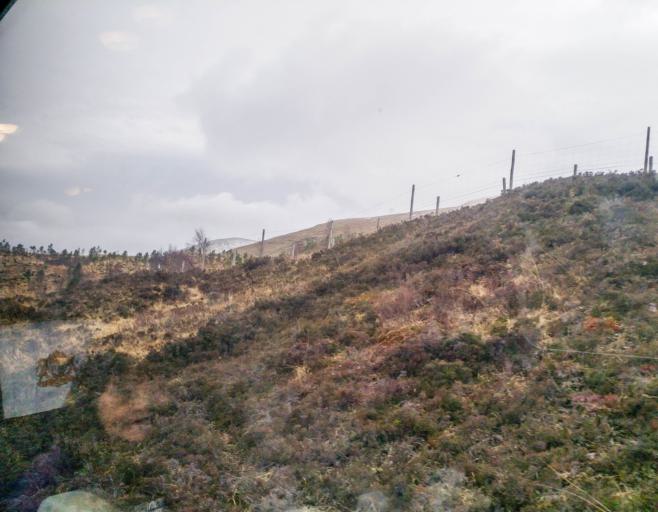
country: GB
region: Scotland
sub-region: Highland
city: Spean Bridge
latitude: 56.5681
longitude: -4.6967
